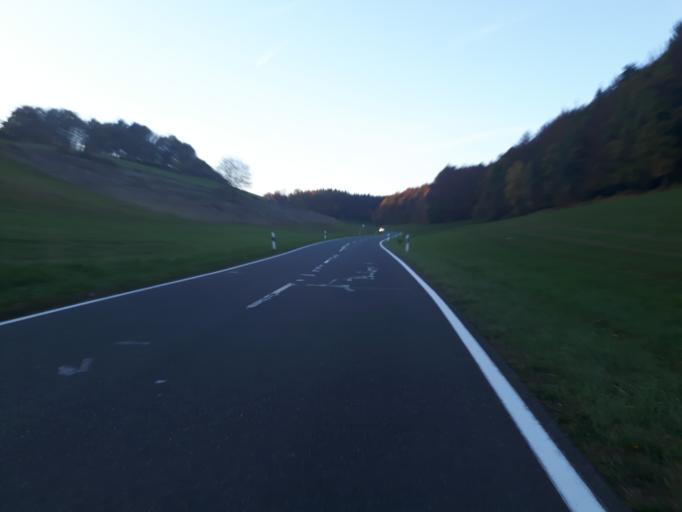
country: DE
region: Bavaria
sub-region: Regierungsbezirk Unterfranken
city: Heimbuchenthal
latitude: 49.8918
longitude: 9.2828
